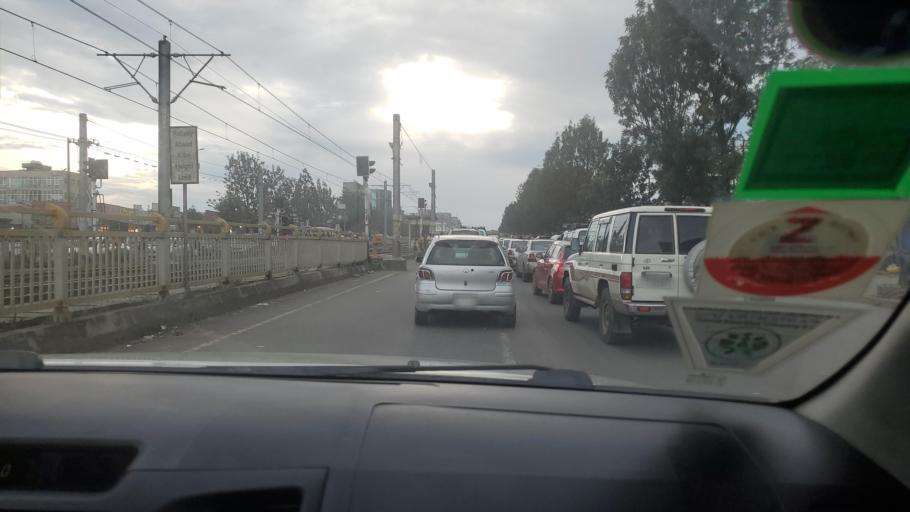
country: ET
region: Adis Abeba
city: Addis Ababa
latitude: 9.0216
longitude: 38.8420
